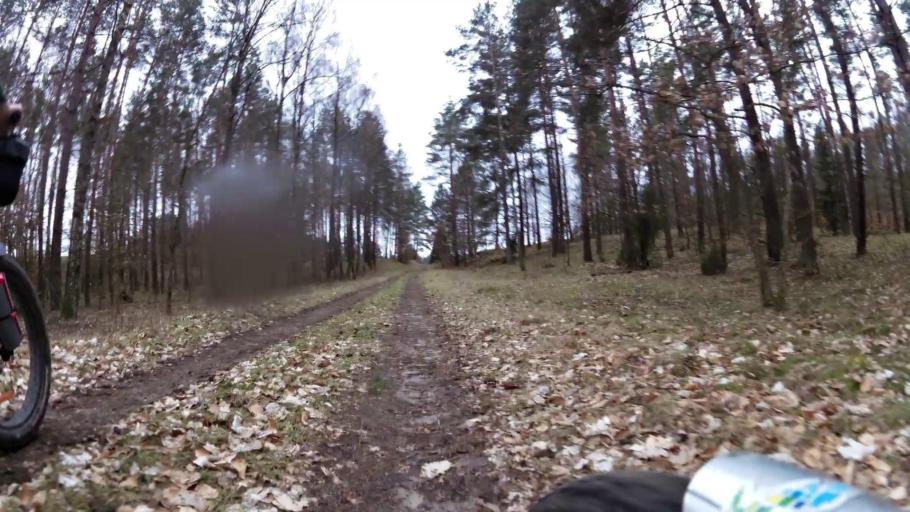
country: PL
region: Pomeranian Voivodeship
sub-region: Powiat bytowski
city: Trzebielino
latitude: 54.0836
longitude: 17.1190
